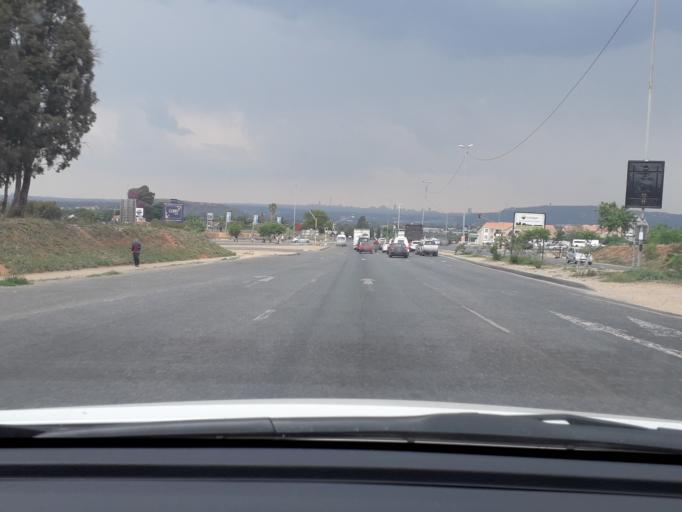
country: ZA
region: Gauteng
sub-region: City of Johannesburg Metropolitan Municipality
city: Roodepoort
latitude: -26.0809
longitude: 27.9307
